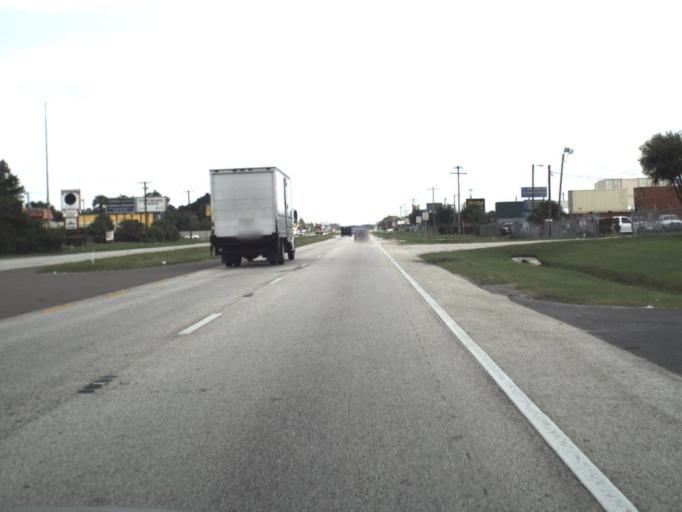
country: US
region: Florida
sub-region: Hillsborough County
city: Palm River-Clair Mel
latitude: 27.9520
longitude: -82.3918
